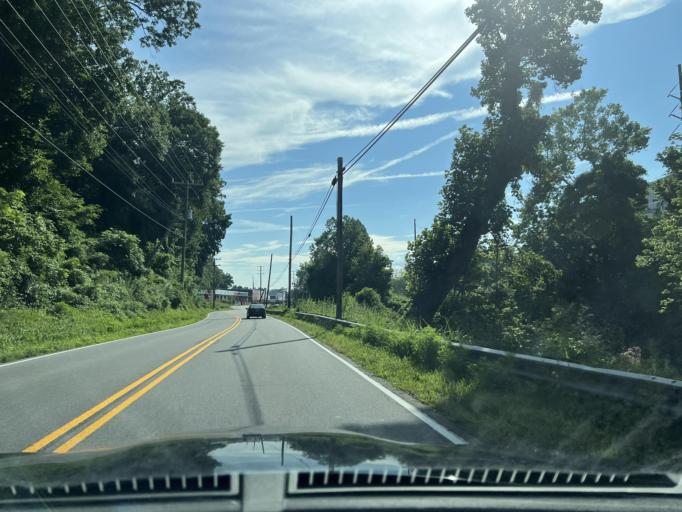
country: US
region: North Carolina
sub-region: Buncombe County
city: Asheville
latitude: 35.5716
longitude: -82.5361
